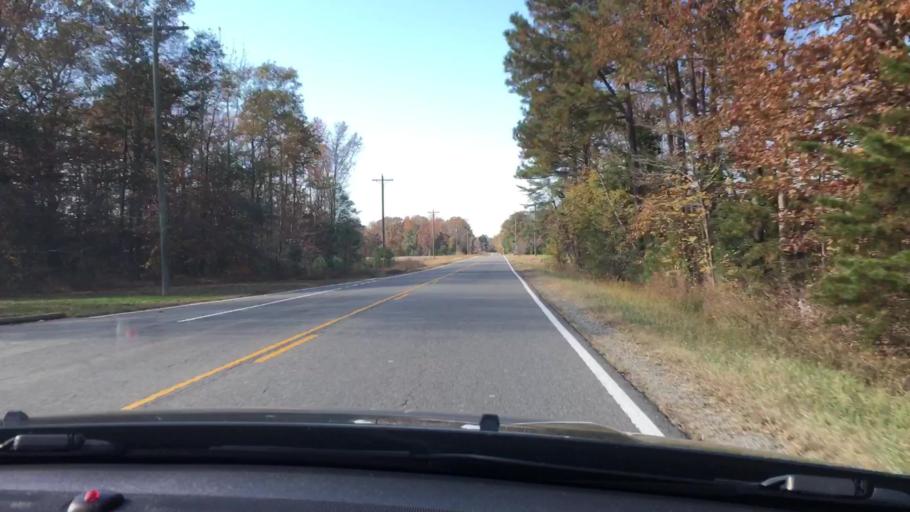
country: US
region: Virginia
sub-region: Hanover County
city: Hanover
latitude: 37.8276
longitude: -77.3452
